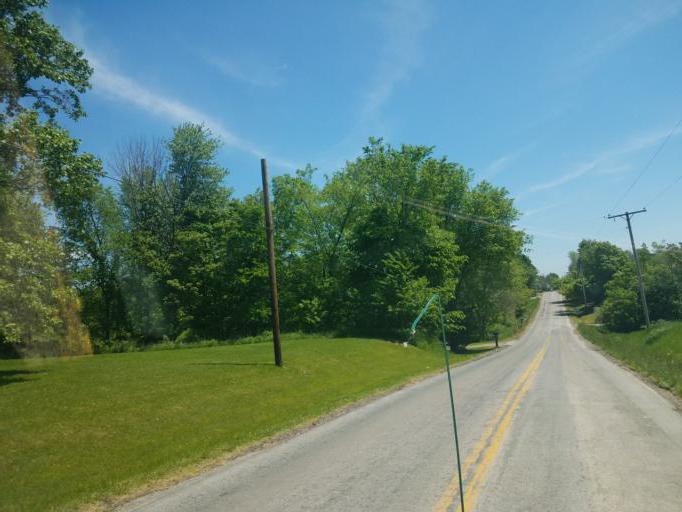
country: US
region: Ohio
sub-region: Wayne County
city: West Salem
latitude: 40.9742
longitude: -82.1697
